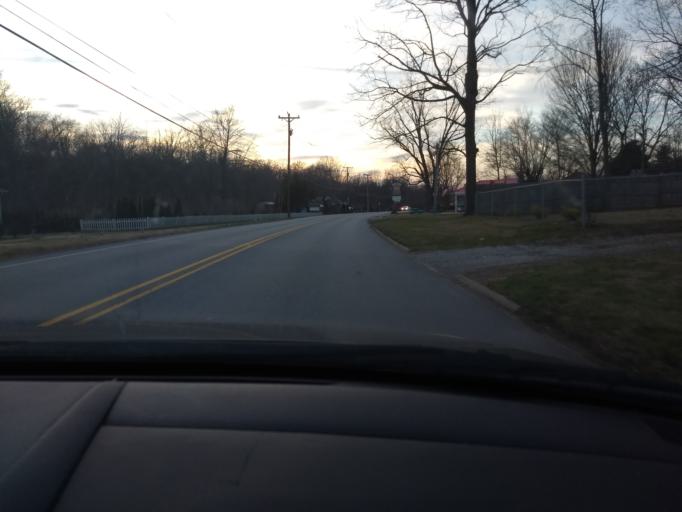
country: US
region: Indiana
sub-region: Floyd County
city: Georgetown
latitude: 38.2946
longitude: -85.9804
